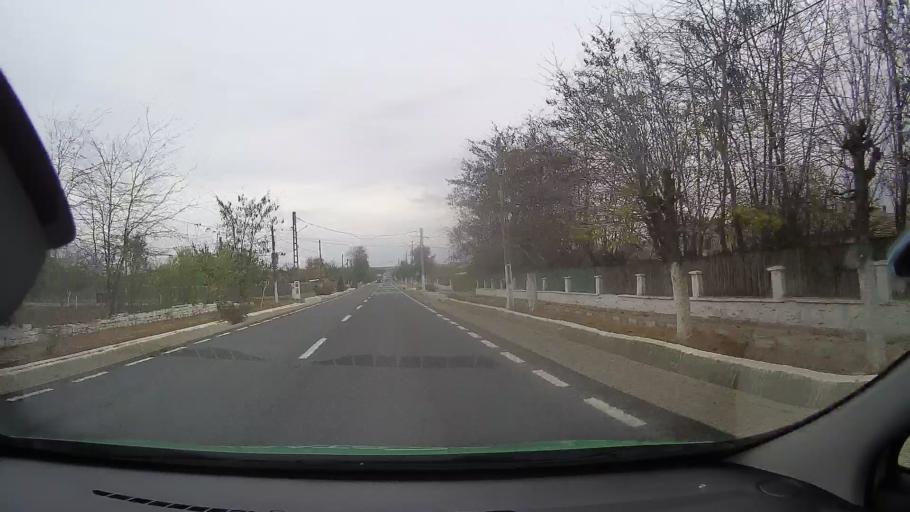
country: RO
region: Constanta
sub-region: Comuna Nicolae Balcescu
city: Nicolae Balcescu
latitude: 44.3893
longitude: 28.3706
